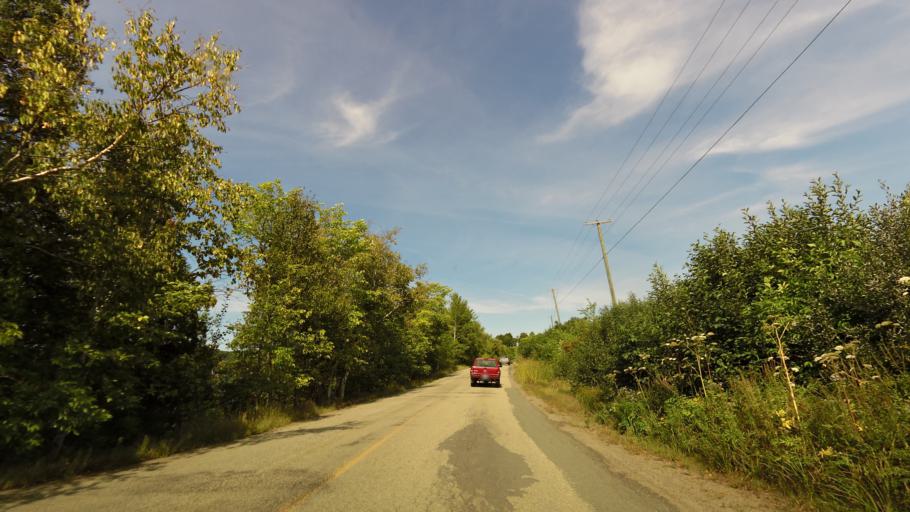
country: CA
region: New Brunswick
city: Hampton
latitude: 45.6046
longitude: -65.9077
